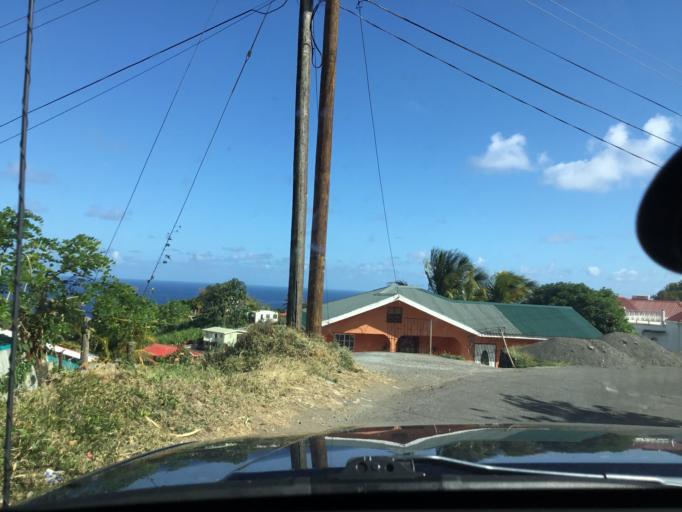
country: VC
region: Charlotte
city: Biabou
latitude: 13.1583
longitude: -61.1577
